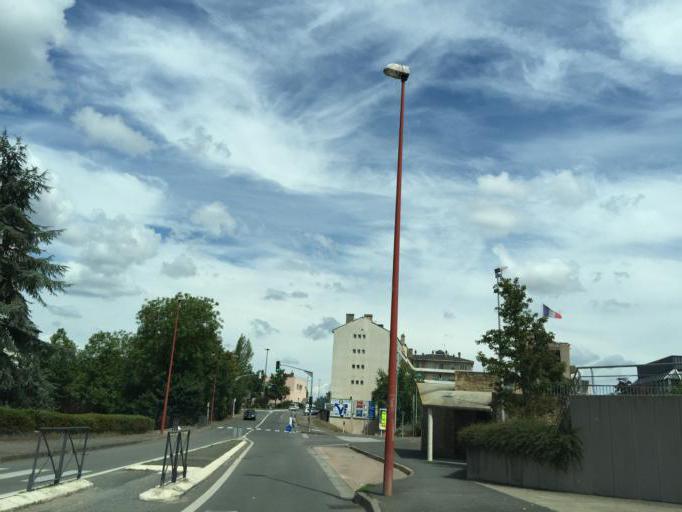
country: FR
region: Midi-Pyrenees
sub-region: Departement de l'Aveyron
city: Rodez
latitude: 44.3599
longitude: 2.5724
